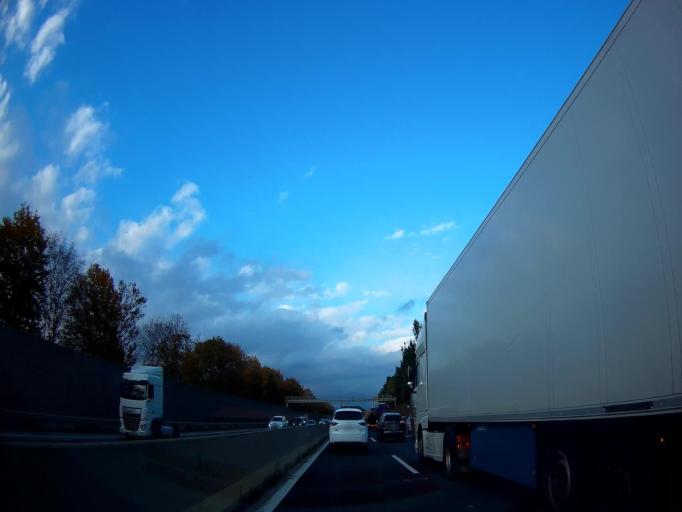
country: AT
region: Styria
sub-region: Politischer Bezirk Graz-Umgebung
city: Seiersberg
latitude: 46.9855
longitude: 15.3971
